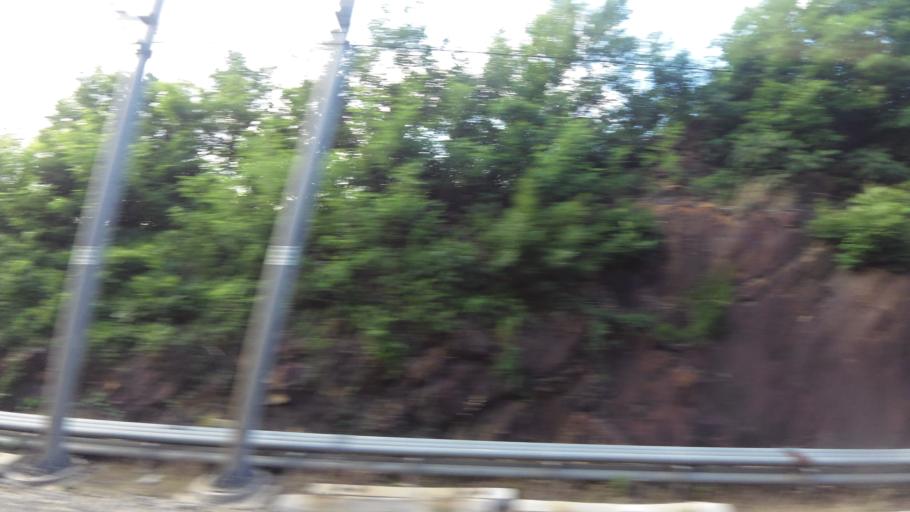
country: KR
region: Chungcheongbuk-do
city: Yong-dong
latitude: 36.1974
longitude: 127.7516
